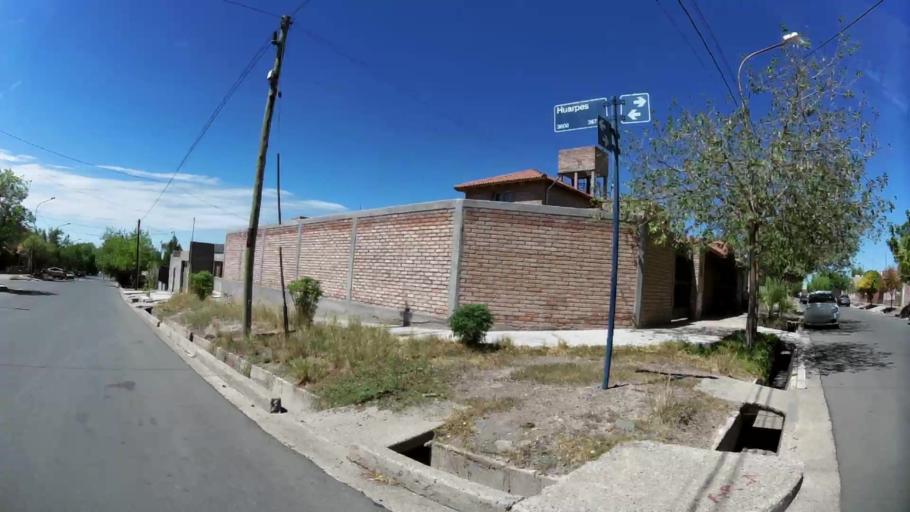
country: AR
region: Mendoza
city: Las Heras
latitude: -32.8458
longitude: -68.8747
